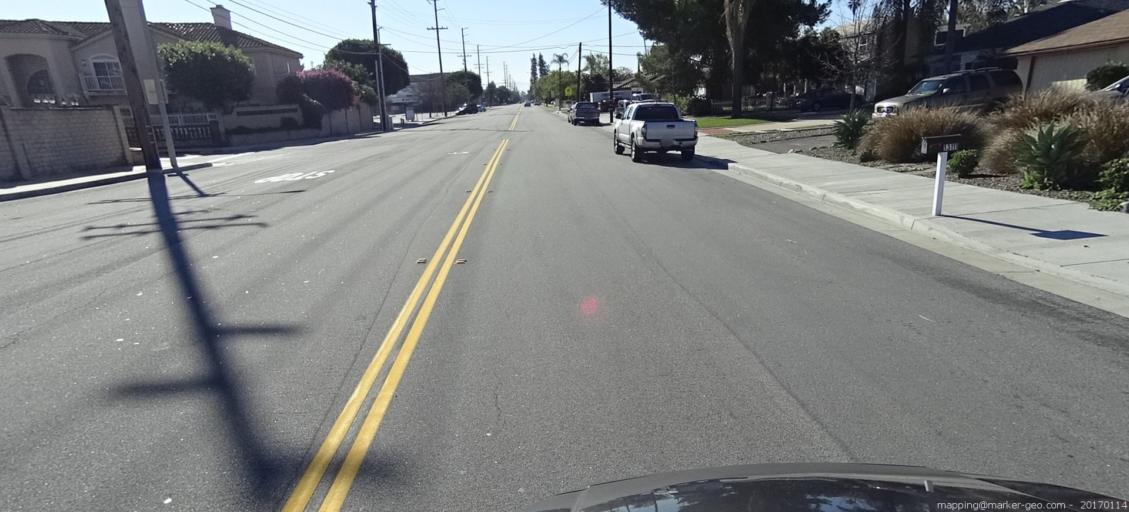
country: US
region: California
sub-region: Orange County
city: North Tustin
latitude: 33.7721
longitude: -117.8055
